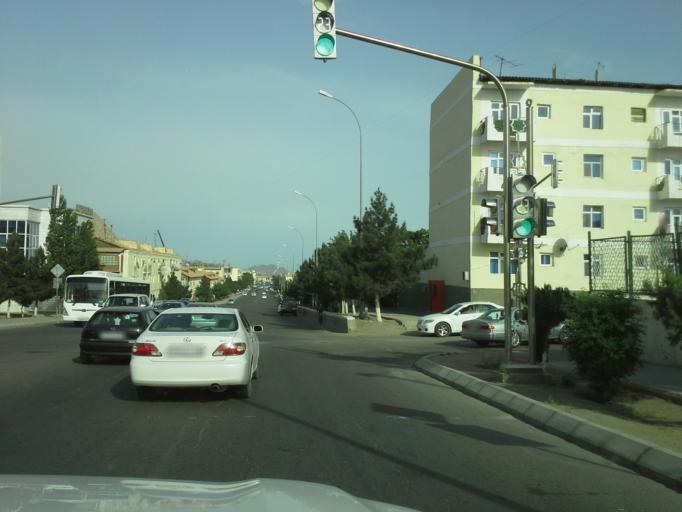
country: TM
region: Balkan
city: Turkmenbasy
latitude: 40.0171
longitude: 52.9765
